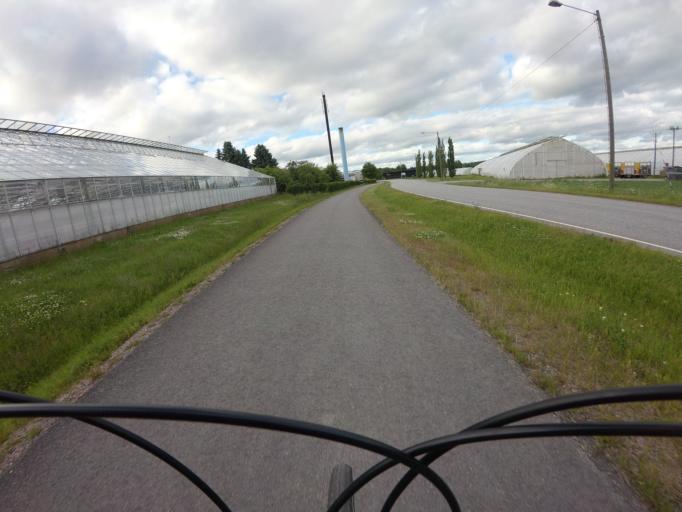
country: FI
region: Varsinais-Suomi
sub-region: Turku
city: Turku
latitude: 60.5034
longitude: 22.3334
